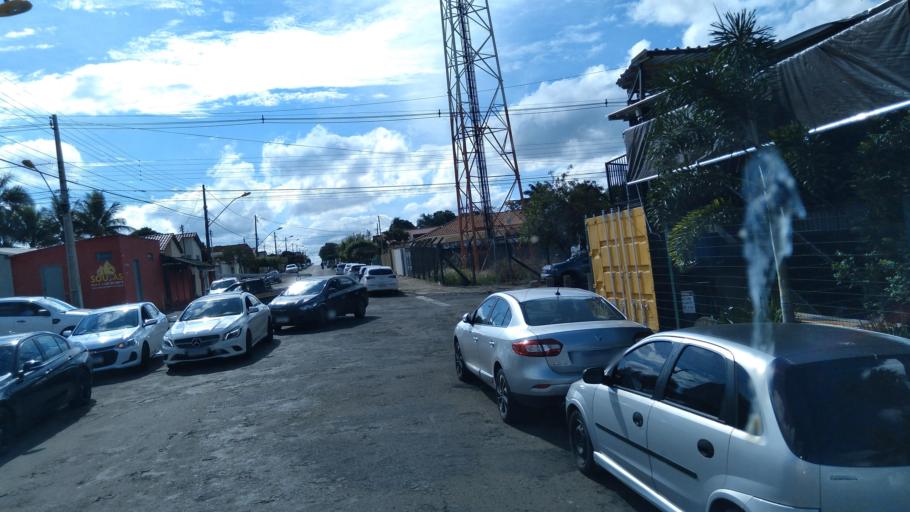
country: BR
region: Goias
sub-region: Mineiros
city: Mineiros
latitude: -17.5594
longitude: -52.5577
